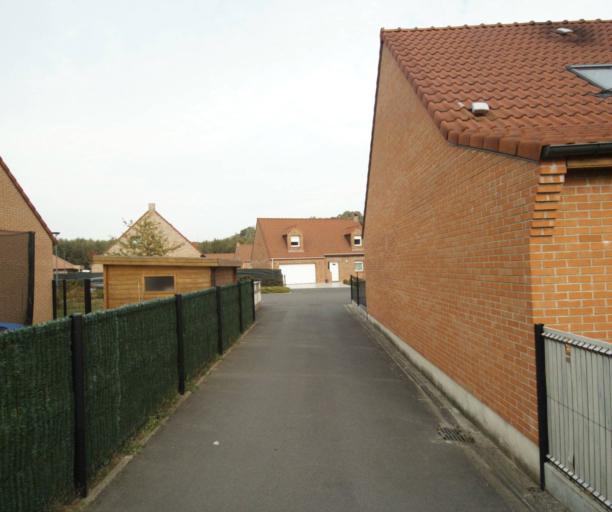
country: FR
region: Nord-Pas-de-Calais
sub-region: Departement du Nord
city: Hallennes-lez-Haubourdin
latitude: 50.6070
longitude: 2.9748
